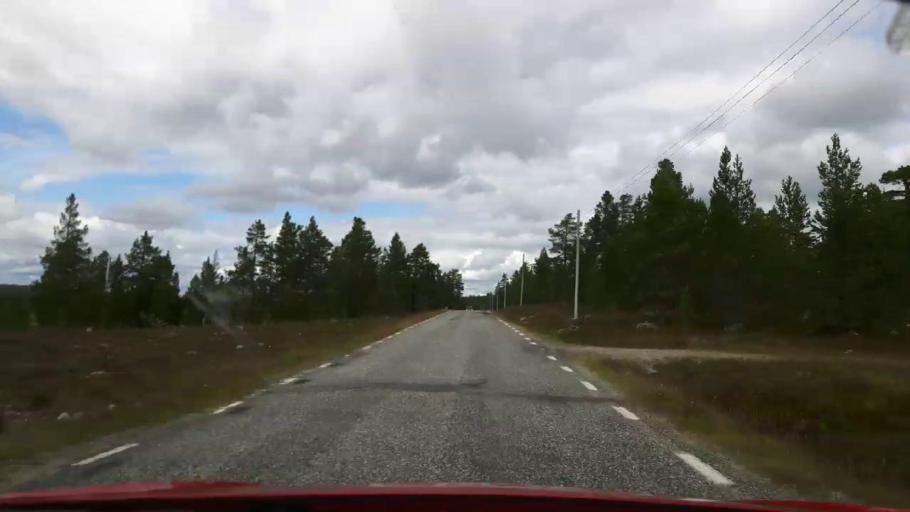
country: NO
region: Hedmark
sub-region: Engerdal
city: Engerdal
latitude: 62.3168
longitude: 12.8085
